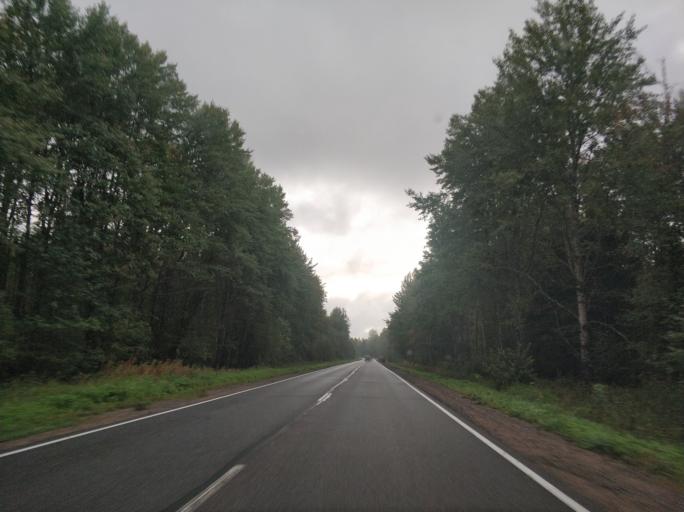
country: RU
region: Leningrad
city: Borisova Griva
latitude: 60.1286
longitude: 30.9632
